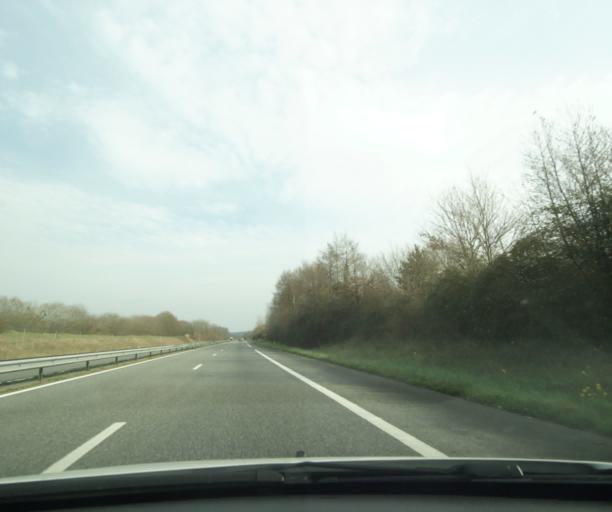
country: FR
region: Aquitaine
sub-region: Departement des Pyrenees-Atlantiques
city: Puyoo
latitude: 43.5099
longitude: -0.8822
